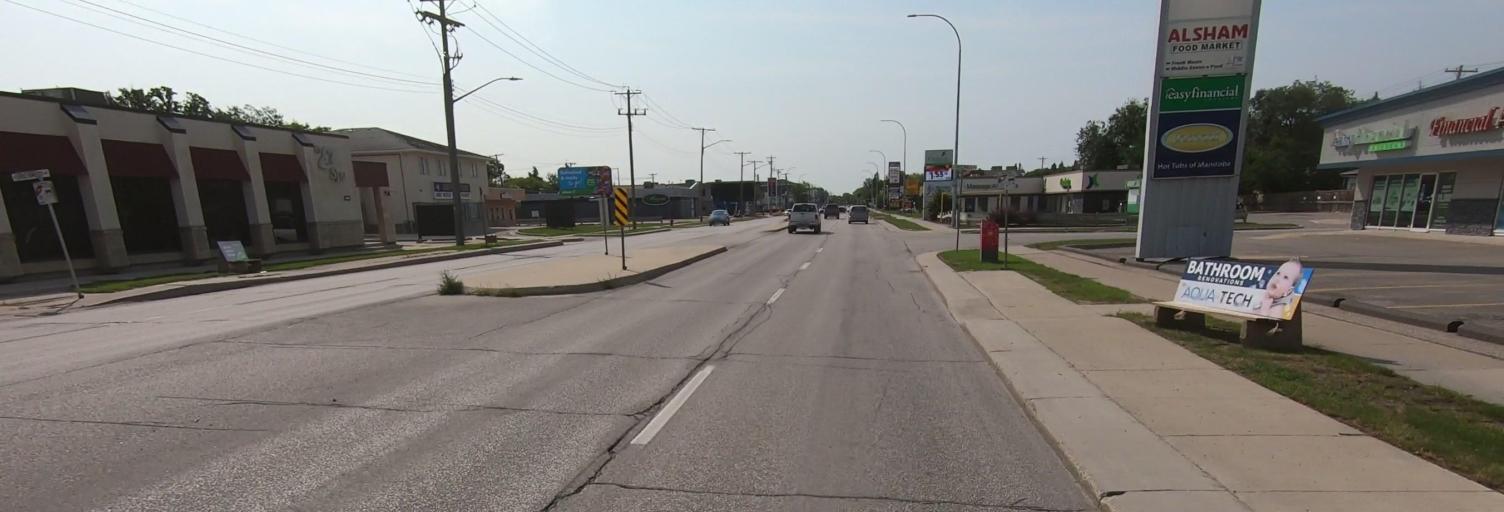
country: CA
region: Manitoba
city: Winnipeg
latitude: 49.8231
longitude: -97.1141
